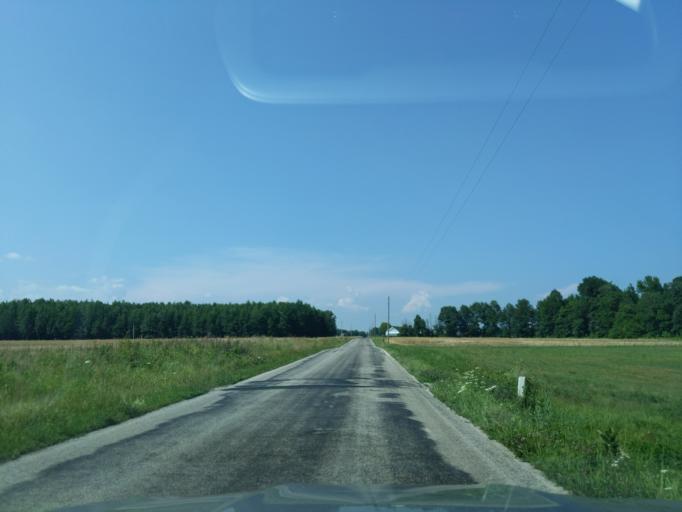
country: US
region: Indiana
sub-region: Ripley County
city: Osgood
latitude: 39.1379
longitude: -85.3399
